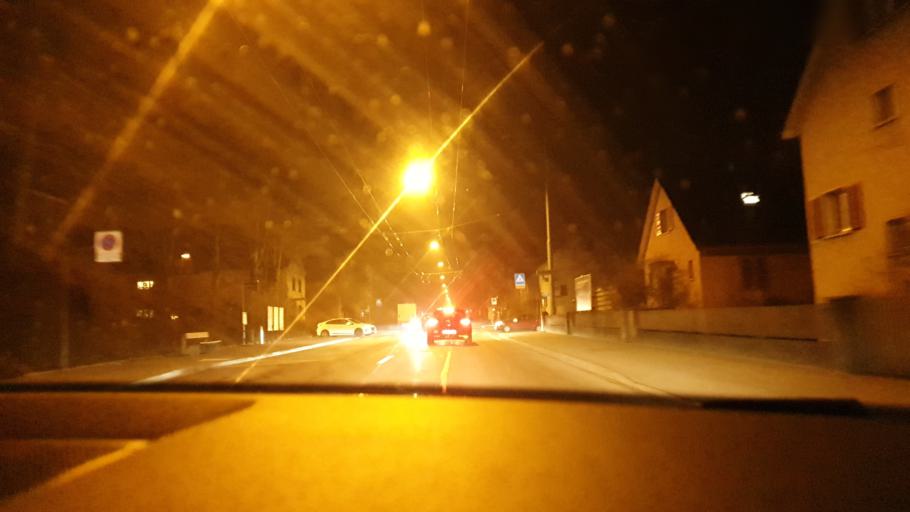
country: CH
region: Zurich
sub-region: Bezirk Winterthur
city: Wuelflingen (Kreis 6) / Haerti
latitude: 47.5141
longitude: 8.6847
